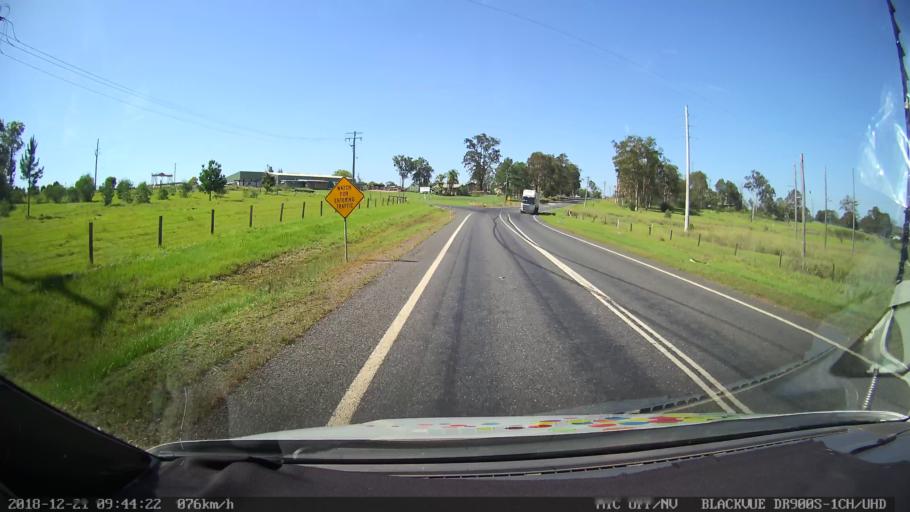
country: AU
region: New South Wales
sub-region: Clarence Valley
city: Grafton
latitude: -29.6172
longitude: 152.9339
